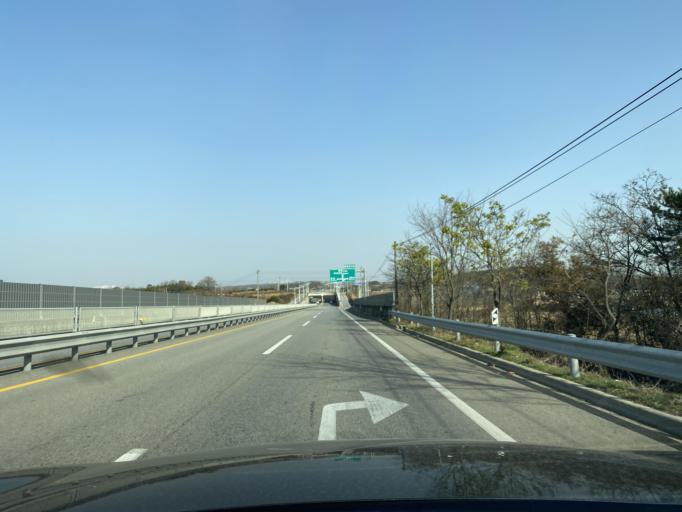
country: KR
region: Chungcheongnam-do
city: Tangjin
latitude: 36.8331
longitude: 126.7537
